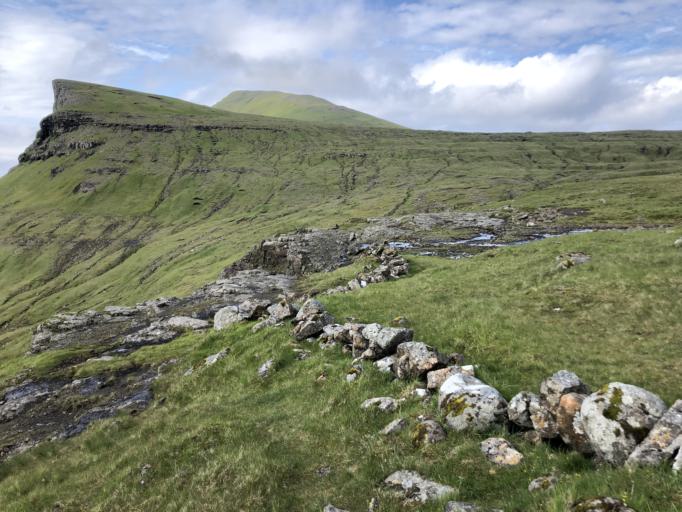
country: FO
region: Streymoy
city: Vestmanna
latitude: 62.2544
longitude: -7.1891
